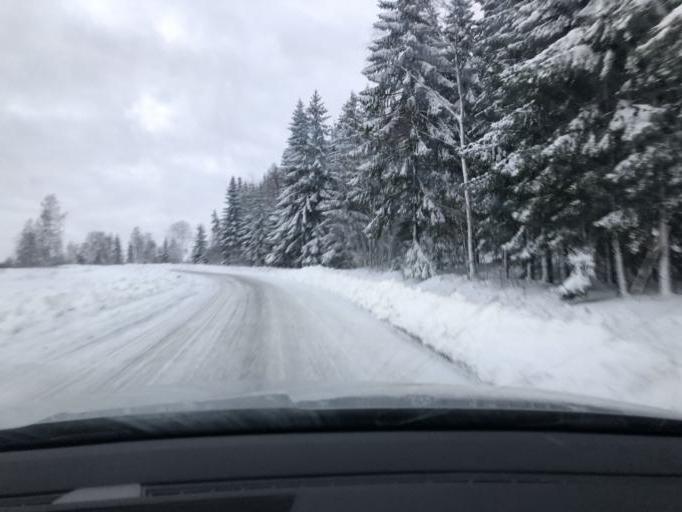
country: SE
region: Vaesternorrland
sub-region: Kramfors Kommun
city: Nordingra
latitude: 62.9165
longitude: 18.2326
